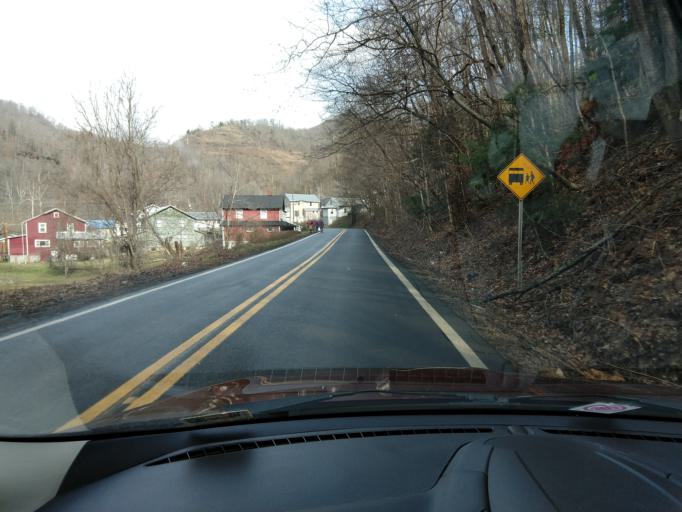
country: US
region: West Virginia
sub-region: McDowell County
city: Welch
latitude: 37.3407
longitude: -81.7243
